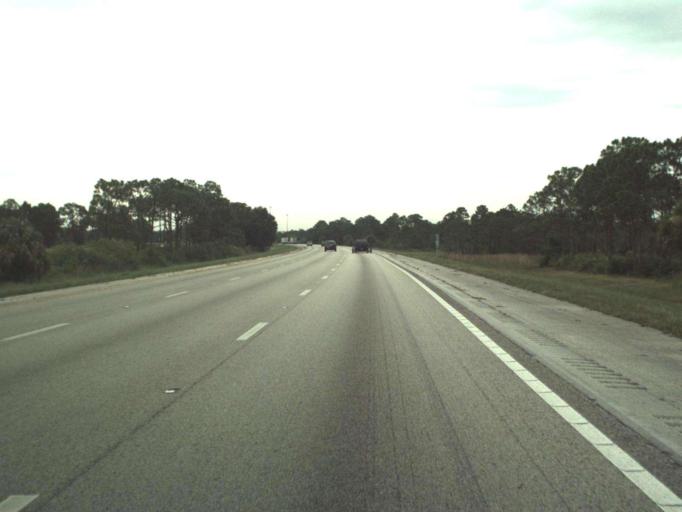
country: US
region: Florida
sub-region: Martin County
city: Palm City
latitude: 27.1310
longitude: -80.3531
